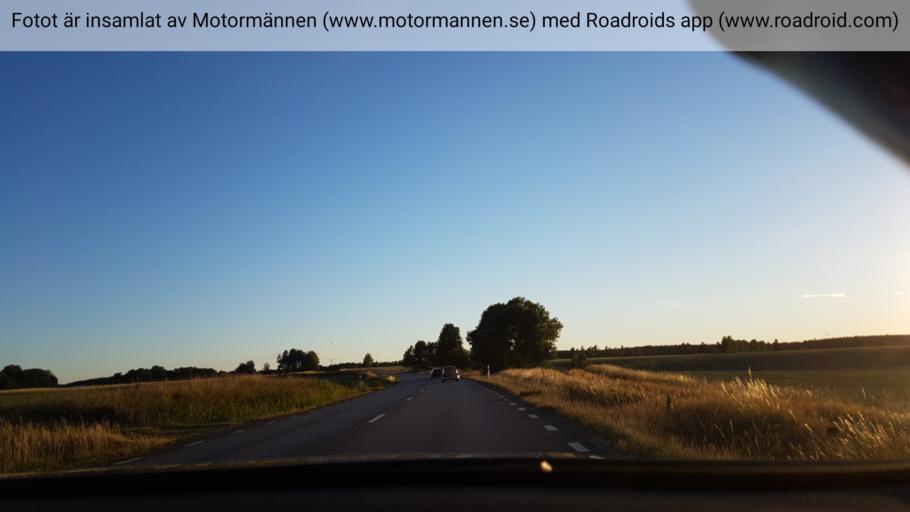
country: SE
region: Vaestra Goetaland
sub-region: Tibro Kommun
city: Tibro
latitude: 58.3470
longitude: 14.1391
